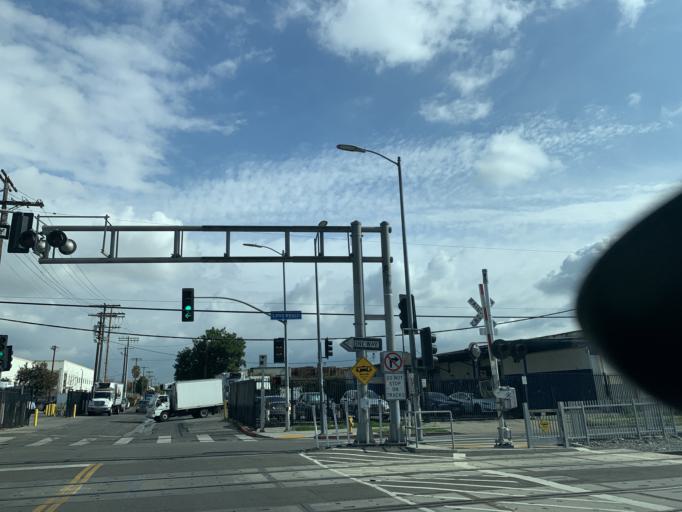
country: US
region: California
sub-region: Los Angeles County
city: Huntington Park
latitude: 33.9994
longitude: -118.2434
